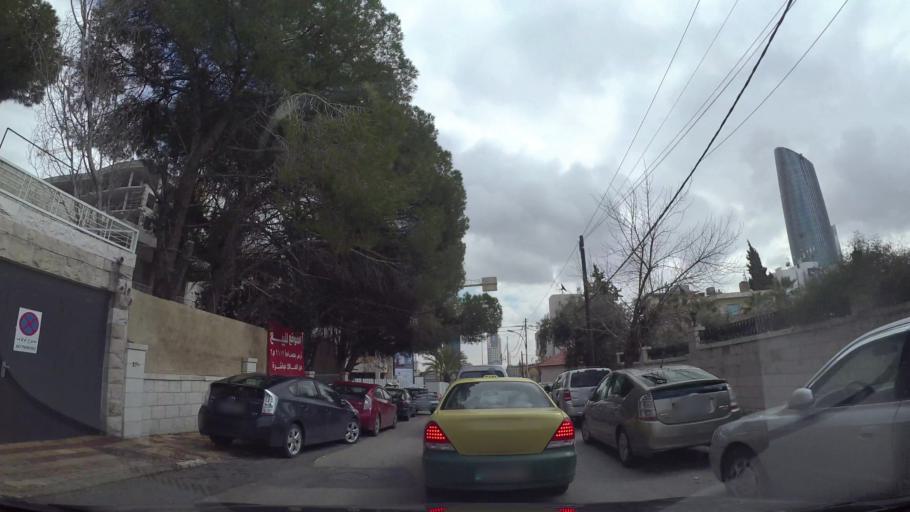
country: JO
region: Amman
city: Amman
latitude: 31.9686
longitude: 35.9029
